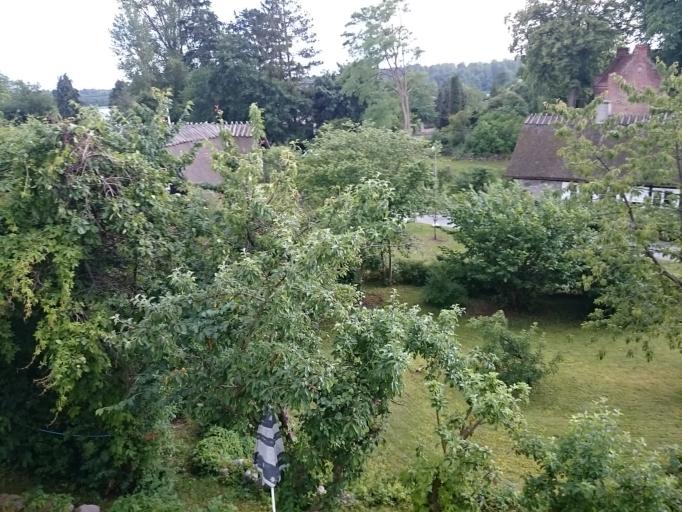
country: DK
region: Capital Region
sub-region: Fureso Kommune
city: Farum
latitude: 55.8074
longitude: 12.3587
